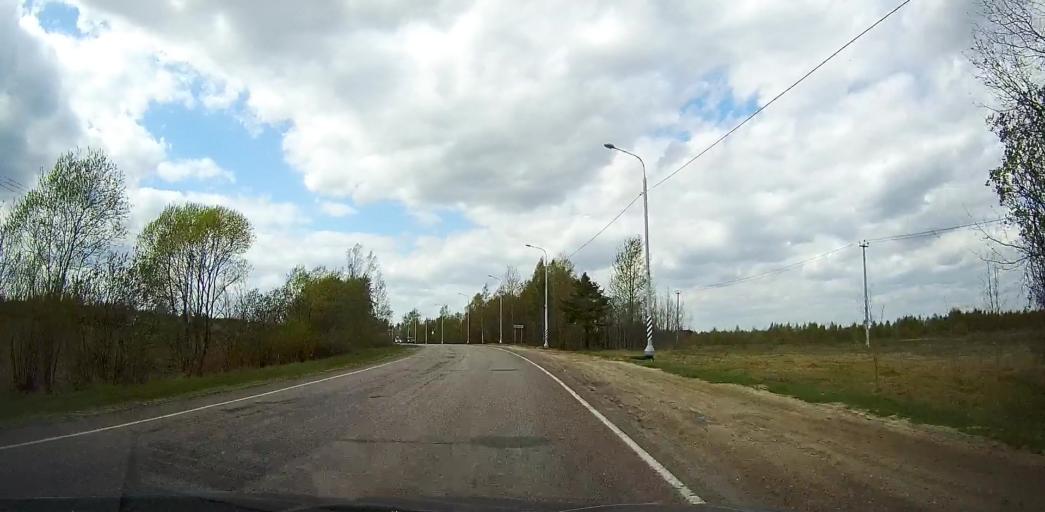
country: RU
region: Moskovskaya
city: Davydovo
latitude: 55.6635
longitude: 38.8049
